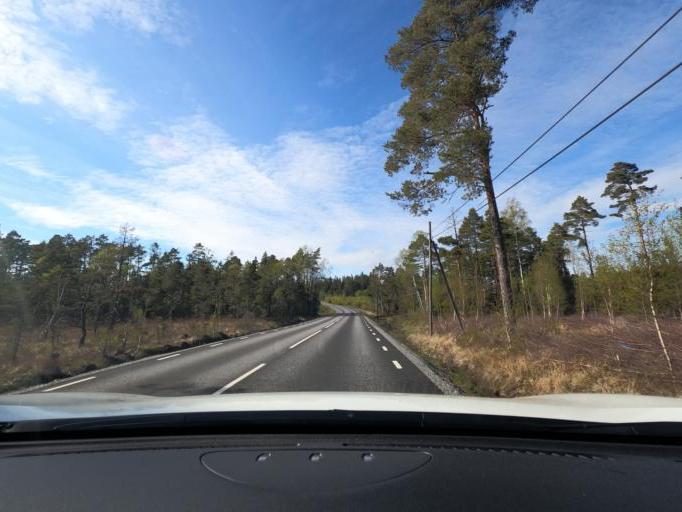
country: SE
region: Vaestra Goetaland
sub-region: Harryda Kommun
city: Landvetter
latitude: 57.6395
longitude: 12.2559
